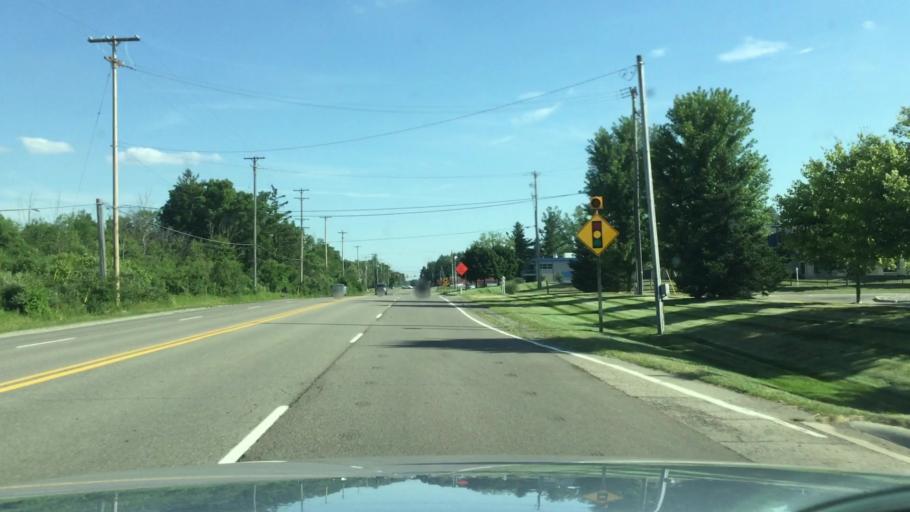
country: US
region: Michigan
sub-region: Genesee County
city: Grand Blanc
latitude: 42.8911
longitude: -83.6000
